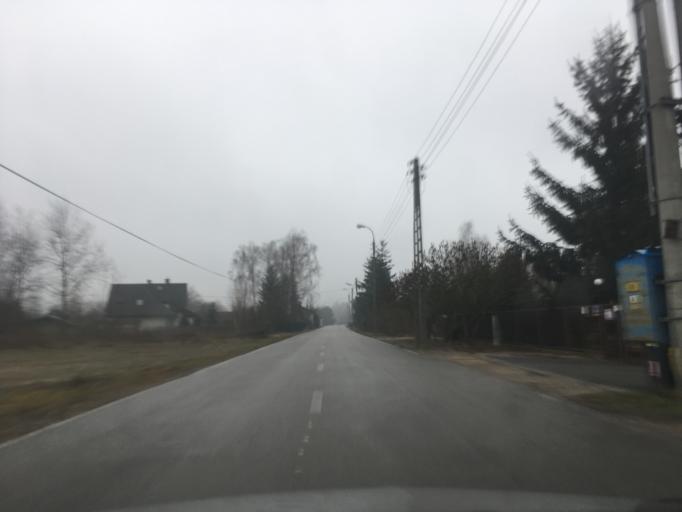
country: PL
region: Masovian Voivodeship
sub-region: Powiat piaseczynski
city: Lesznowola
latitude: 52.0578
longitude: 20.9084
